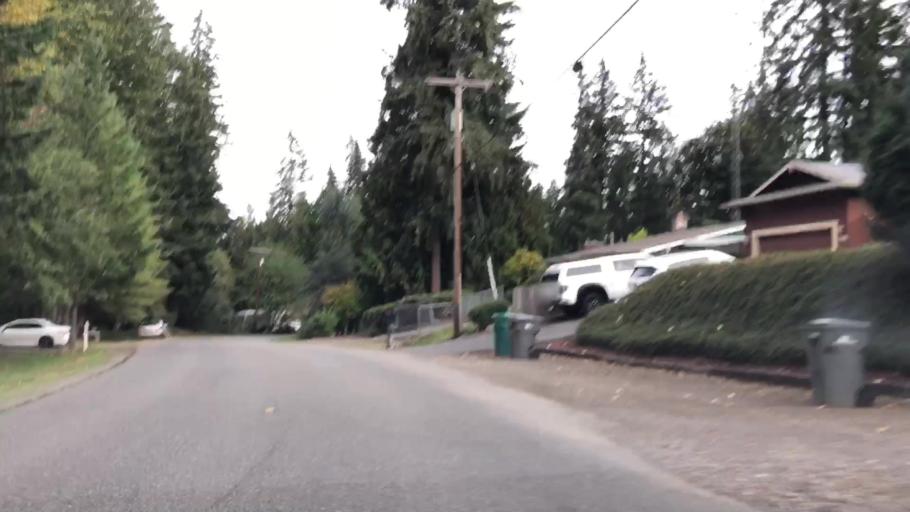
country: US
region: Washington
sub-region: King County
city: Cottage Lake
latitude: 47.7434
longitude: -122.1011
